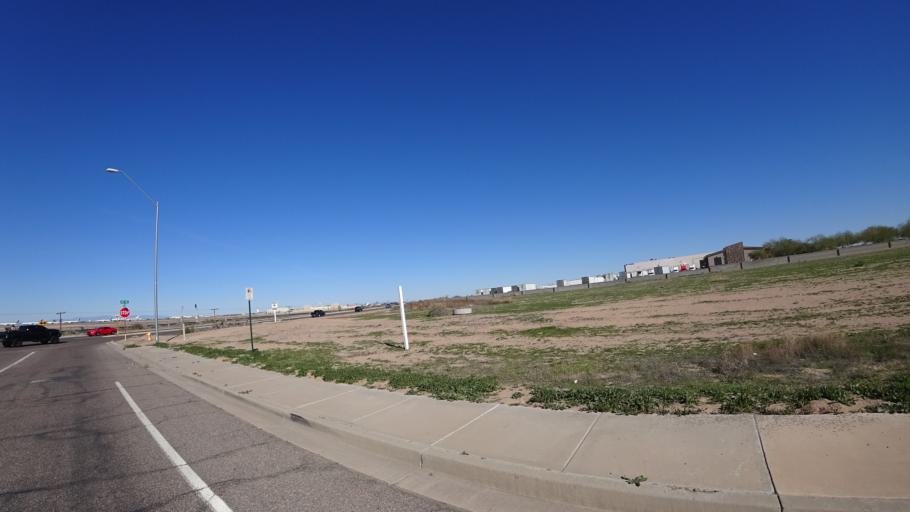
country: US
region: Arizona
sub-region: Maricopa County
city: Goodyear
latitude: 33.4144
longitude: -112.3750
